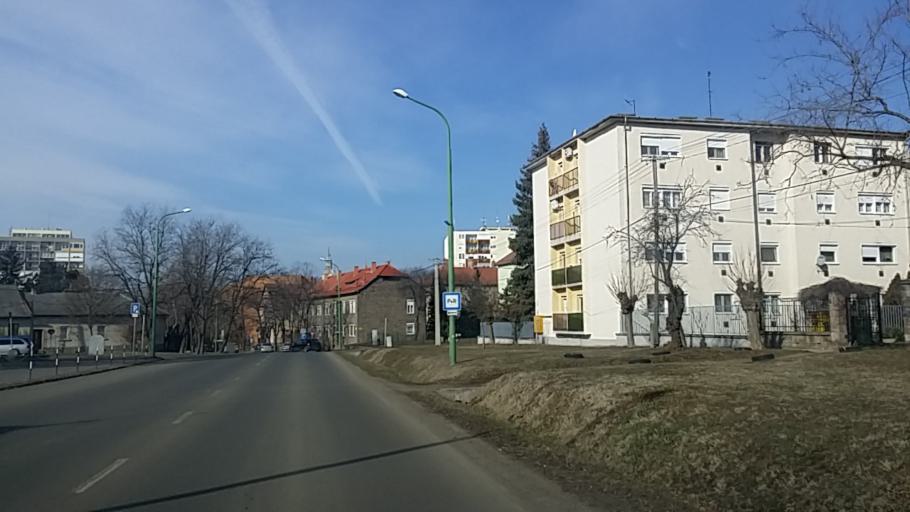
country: HU
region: Heves
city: Gyongyos
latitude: 47.7806
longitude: 19.9338
